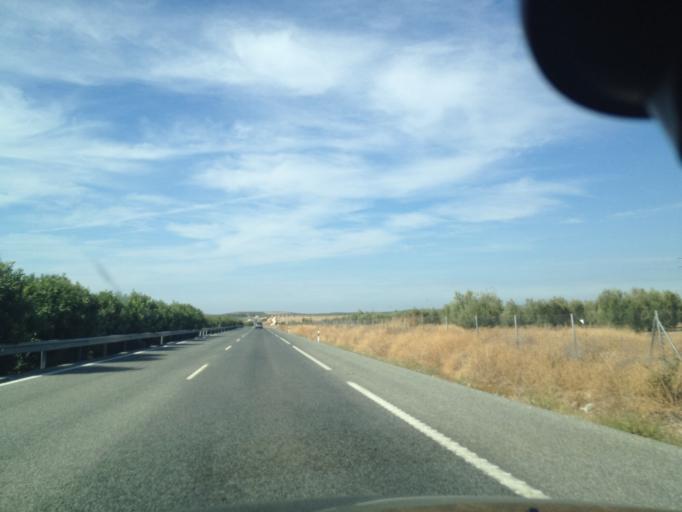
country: ES
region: Andalusia
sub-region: Provincia de Sevilla
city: La Puebla de Cazalla
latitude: 37.2324
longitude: -5.2271
